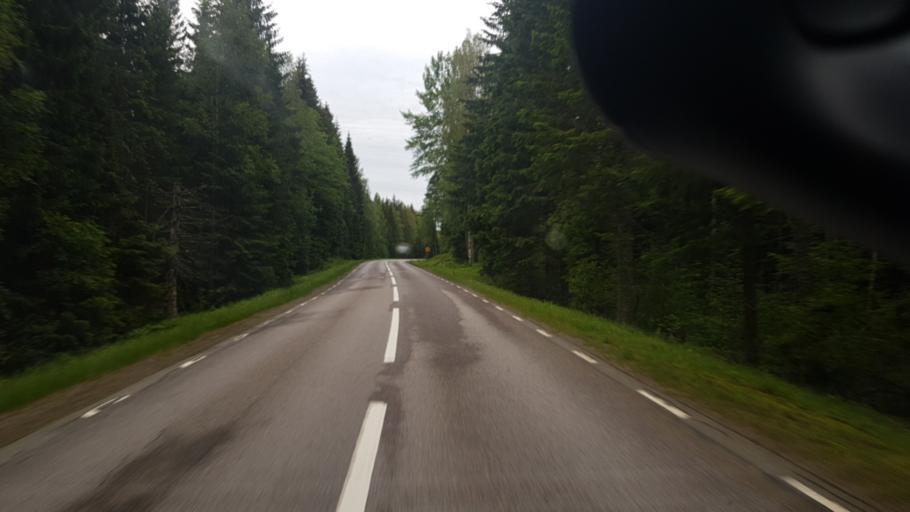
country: SE
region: Vaermland
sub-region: Eda Kommun
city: Amotfors
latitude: 59.6448
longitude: 12.3560
